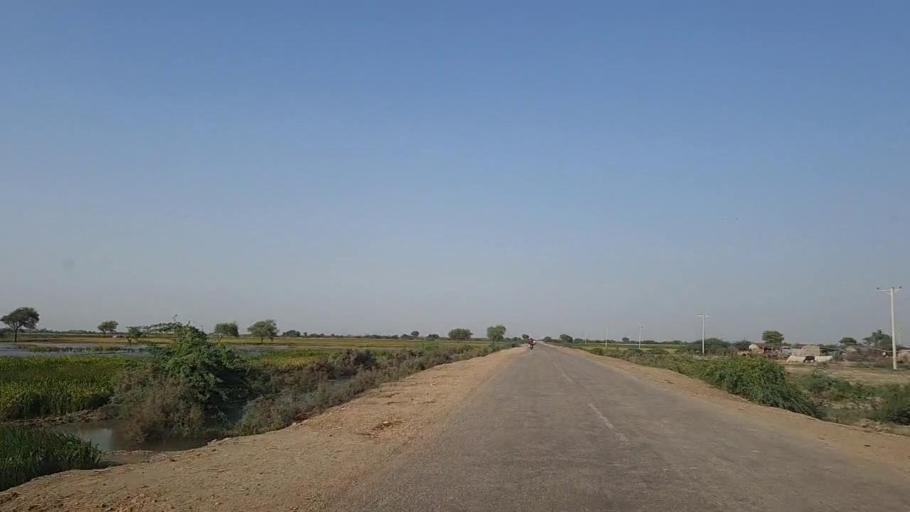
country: PK
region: Sindh
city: Mirpur Batoro
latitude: 24.5947
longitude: 68.3992
